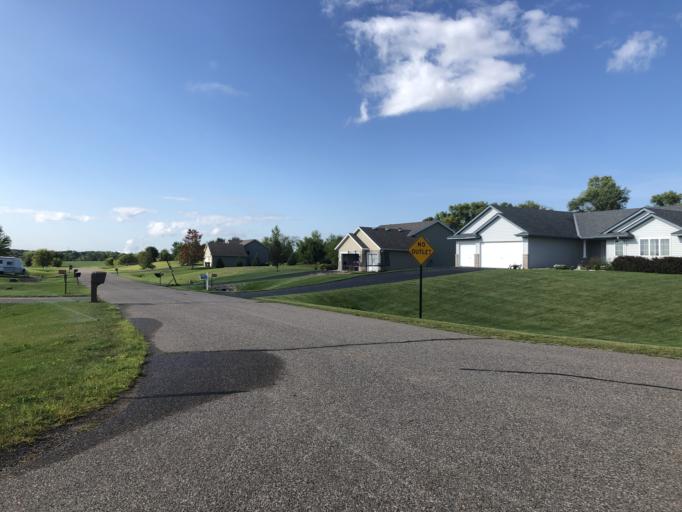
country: US
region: Minnesota
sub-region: Sherburne County
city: Becker
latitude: 45.4236
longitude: -93.8359
